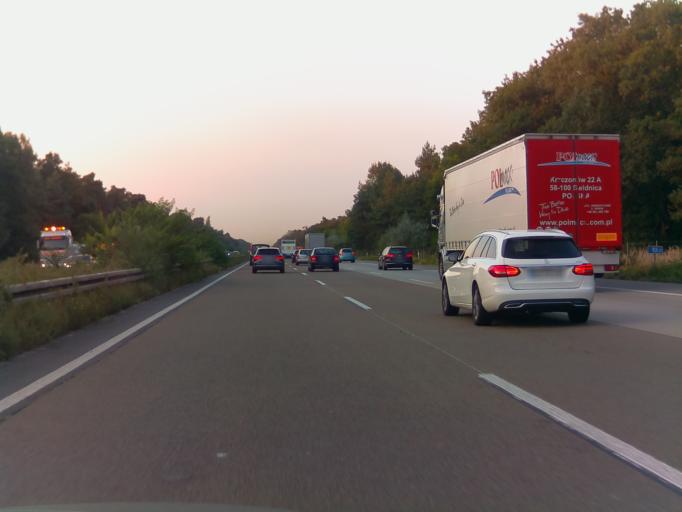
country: DE
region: Hesse
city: Lorsch
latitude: 49.6072
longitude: 8.5585
